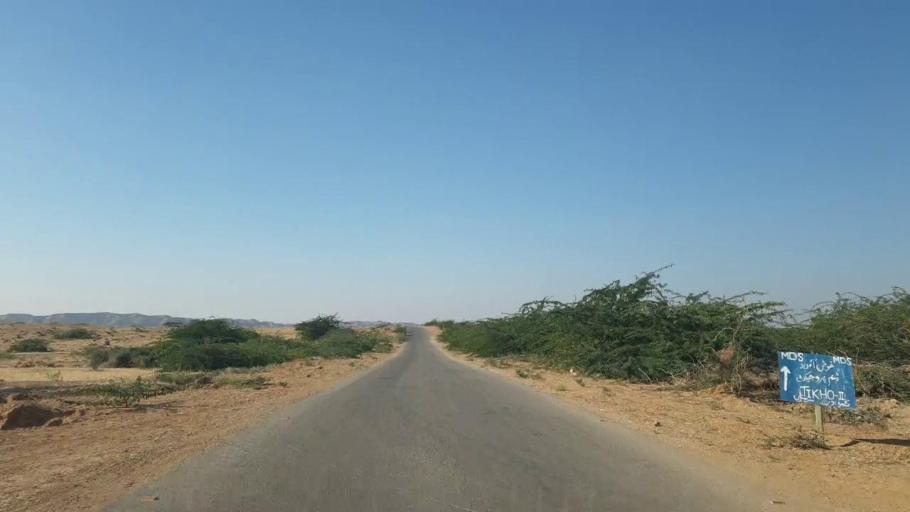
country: PK
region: Sindh
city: Malir Cantonment
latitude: 25.2808
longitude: 67.5837
